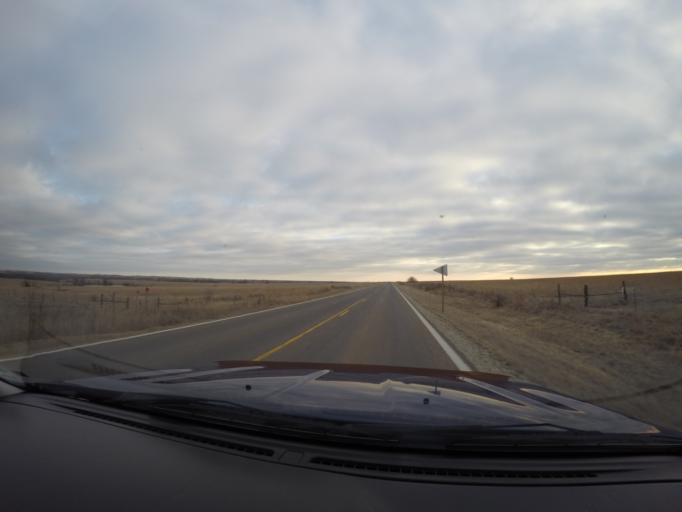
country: US
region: Kansas
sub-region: Morris County
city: Council Grove
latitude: 38.7610
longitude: -96.5012
